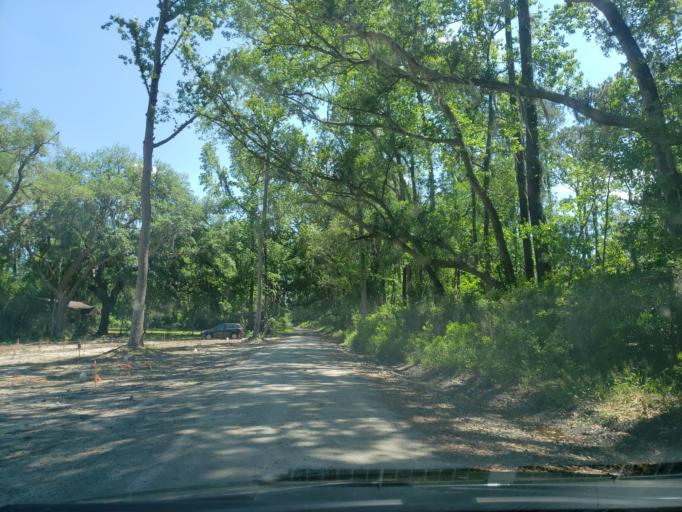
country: US
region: Georgia
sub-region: Chatham County
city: Whitemarsh Island
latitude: 32.0533
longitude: -81.0193
